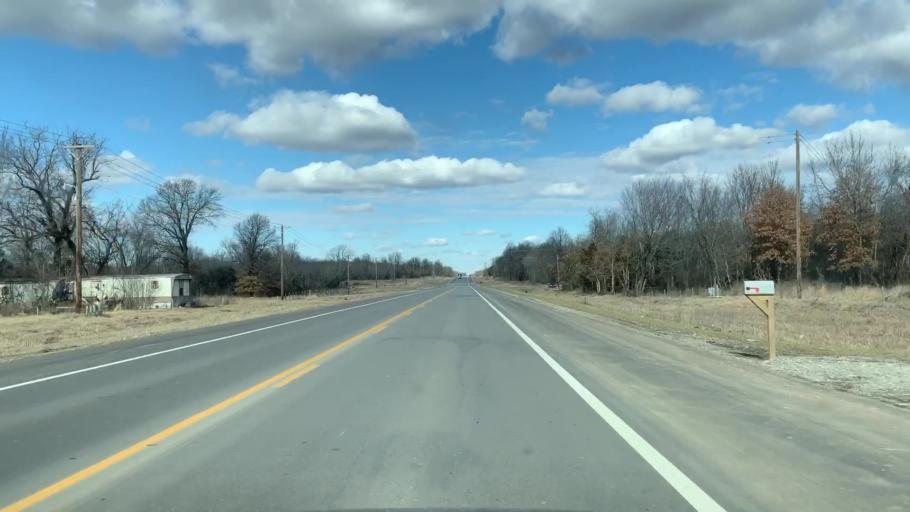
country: US
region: Kansas
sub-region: Cherokee County
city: Columbus
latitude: 37.2234
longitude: -94.8319
